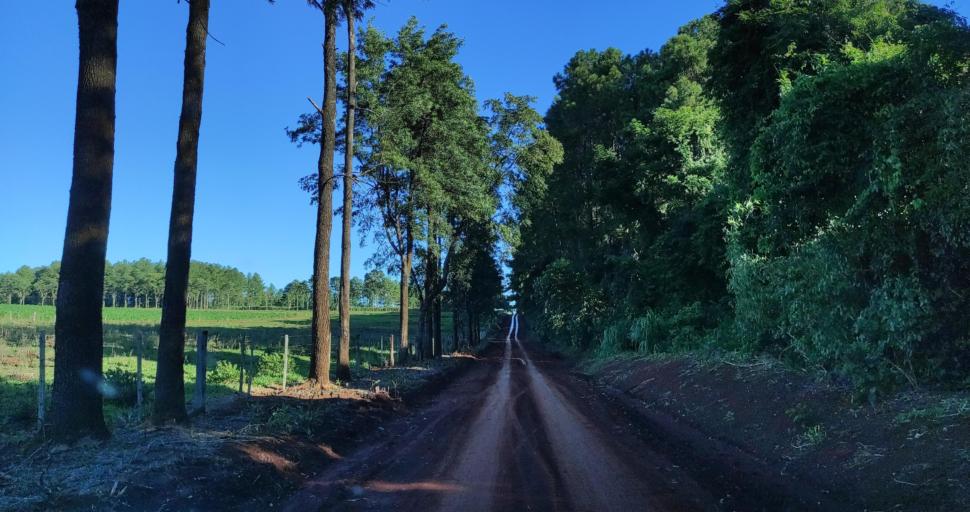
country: AR
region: Misiones
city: Puerto Rico
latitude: -26.8404
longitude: -55.0126
